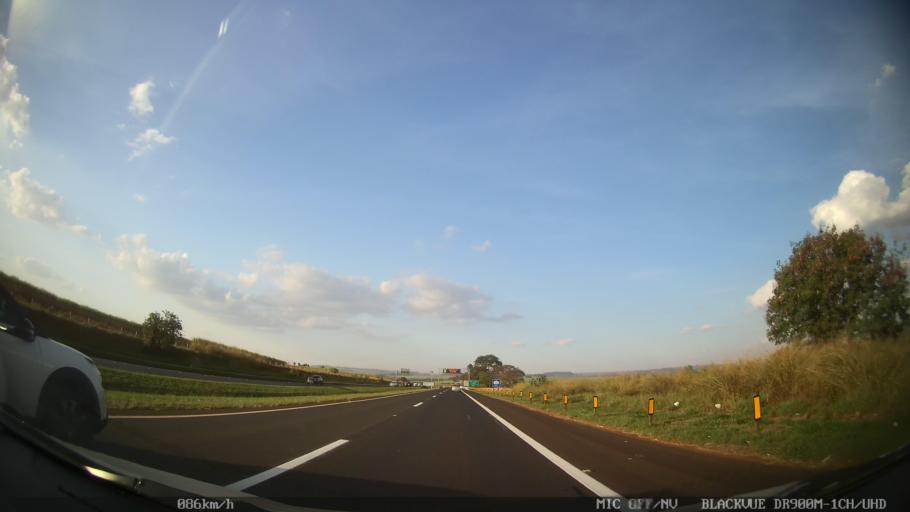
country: BR
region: Sao Paulo
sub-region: Ribeirao Preto
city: Ribeirao Preto
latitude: -21.1099
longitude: -47.7737
